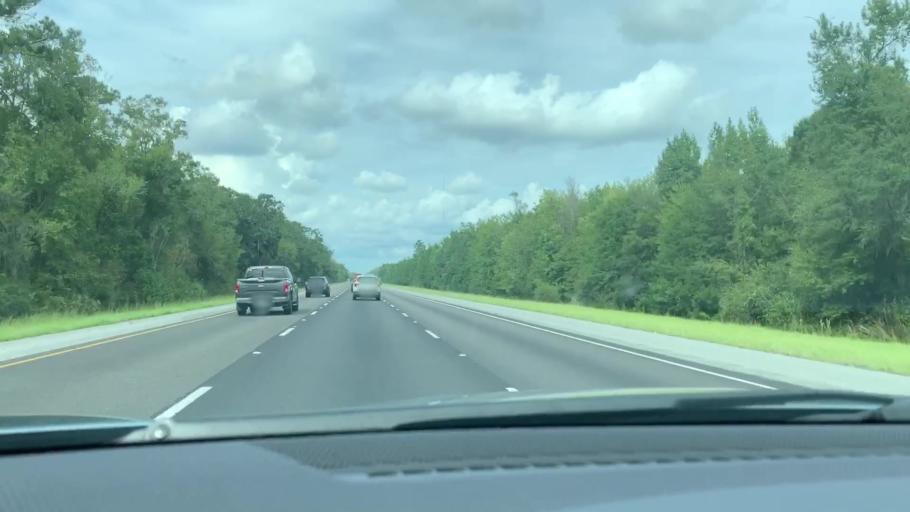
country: US
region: Georgia
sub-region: Liberty County
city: Midway
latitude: 31.6845
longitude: -81.3915
